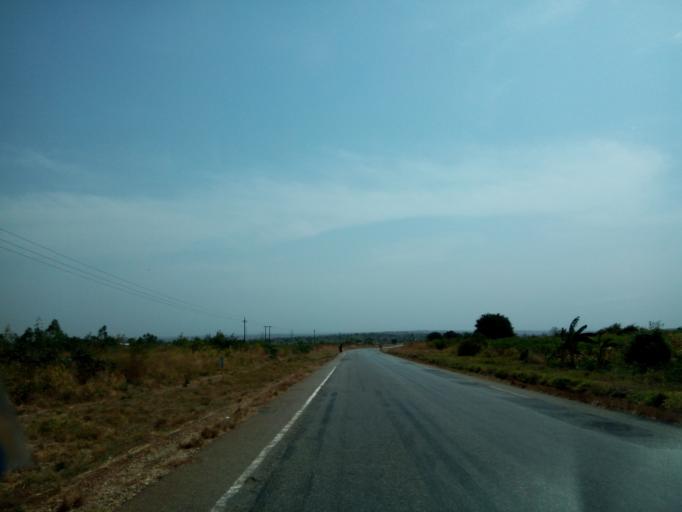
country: UG
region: Northern Region
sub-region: Nebbi District
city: Nebbi
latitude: 2.4632
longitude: 31.2968
